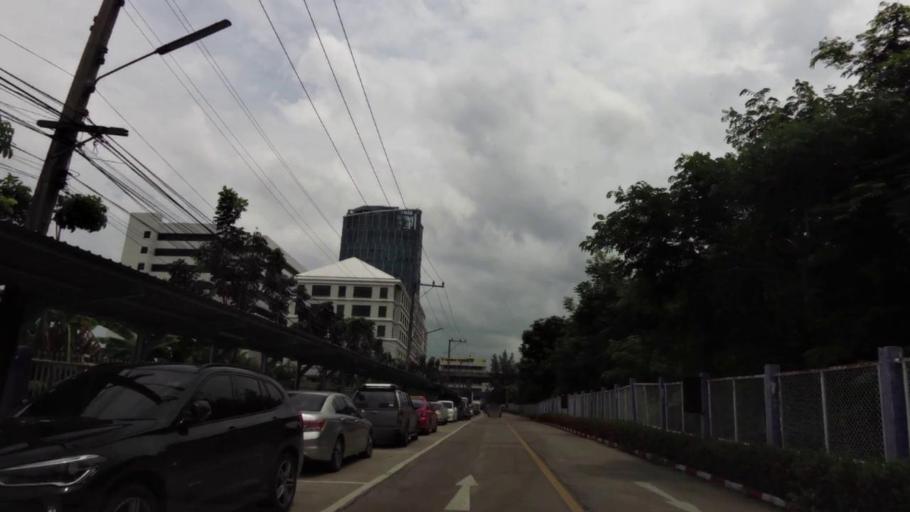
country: TH
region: Bangkok
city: Phra Khanong
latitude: 13.6958
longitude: 100.6080
